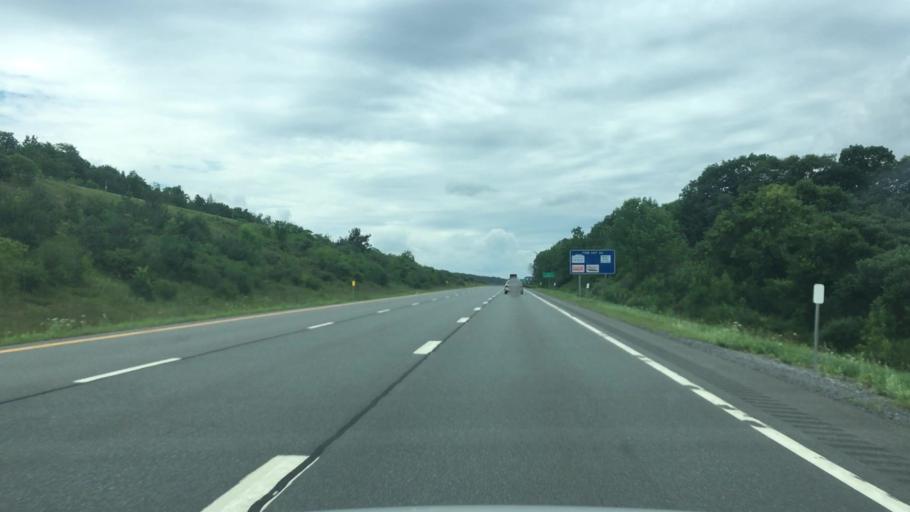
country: US
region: New York
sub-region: Albany County
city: Altamont
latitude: 42.7679
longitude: -74.1016
